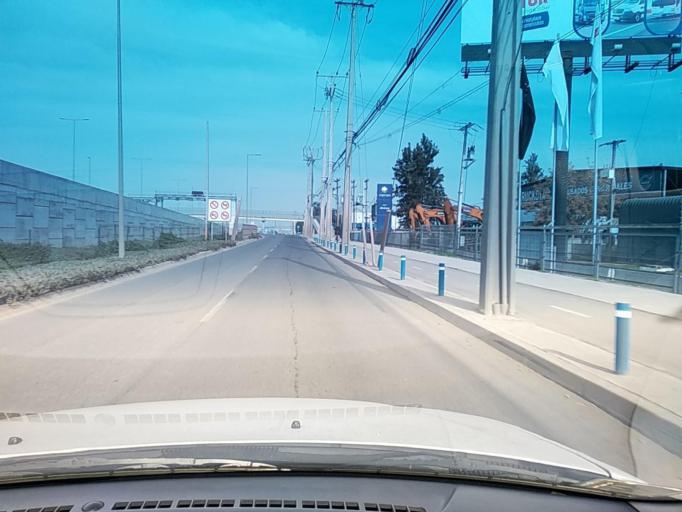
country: CL
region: Santiago Metropolitan
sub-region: Provincia de Chacabuco
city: Chicureo Abajo
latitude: -33.3160
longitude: -70.7233
